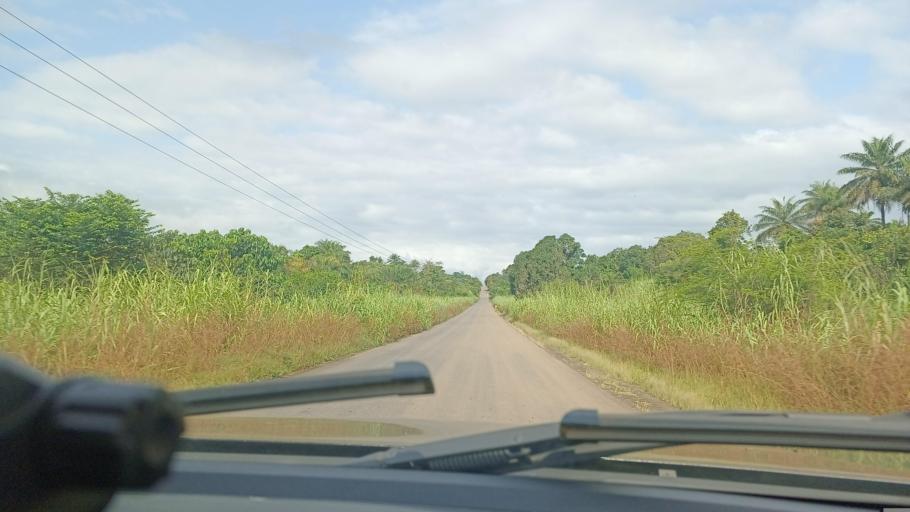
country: LR
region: Bomi
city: Tubmanburg
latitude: 6.7057
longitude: -10.9242
